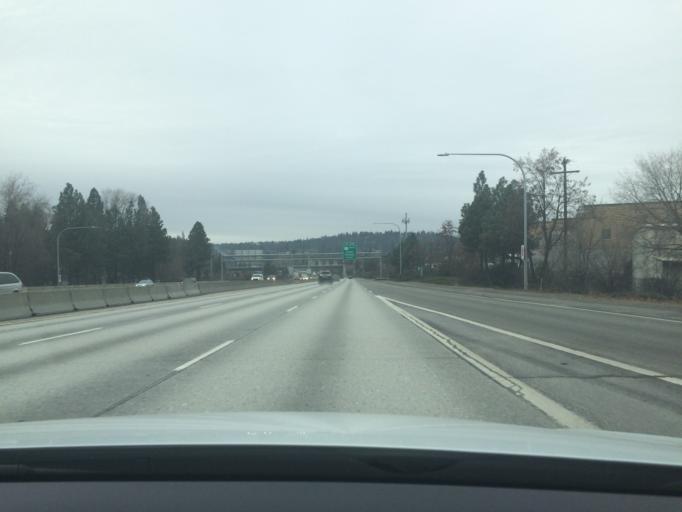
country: US
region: Washington
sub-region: Spokane County
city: Spokane
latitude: 47.6506
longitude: -117.4393
